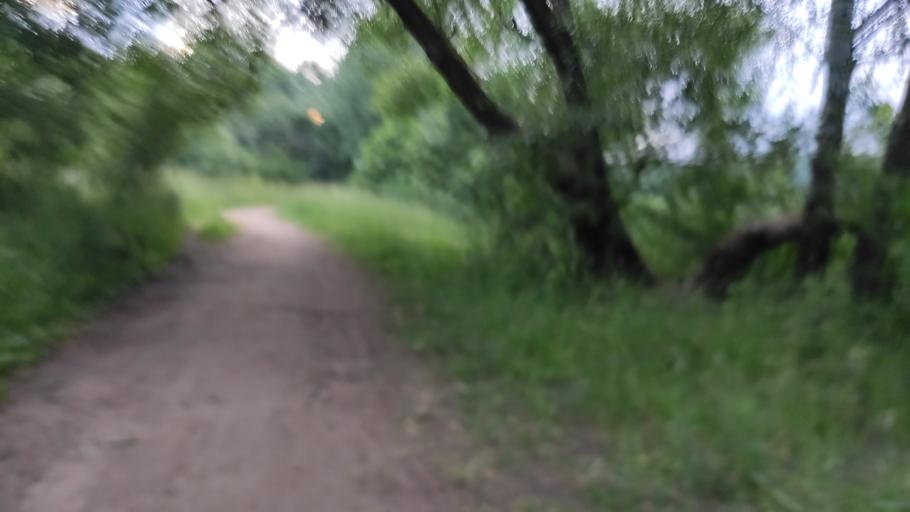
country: BY
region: Minsk
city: Zhdanovichy
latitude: 53.9628
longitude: 27.4429
